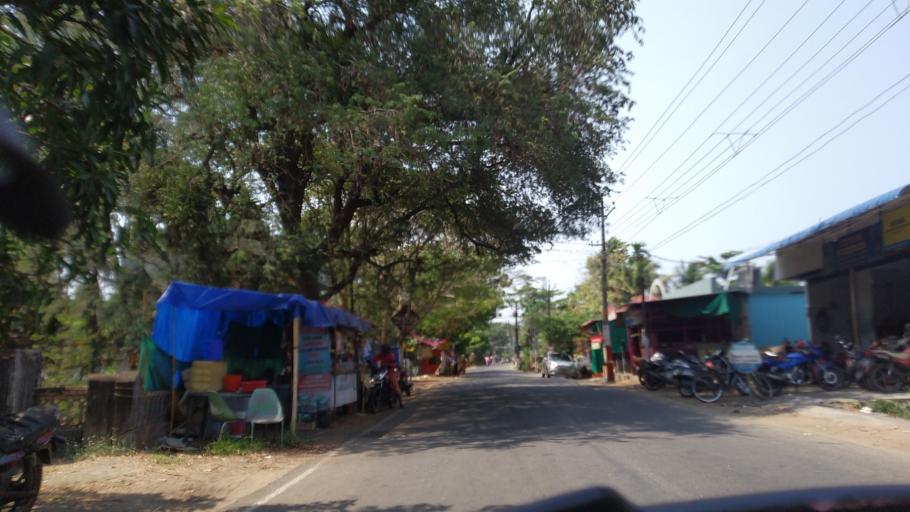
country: IN
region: Kerala
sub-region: Thrissur District
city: Kodungallur
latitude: 10.2146
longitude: 76.1612
